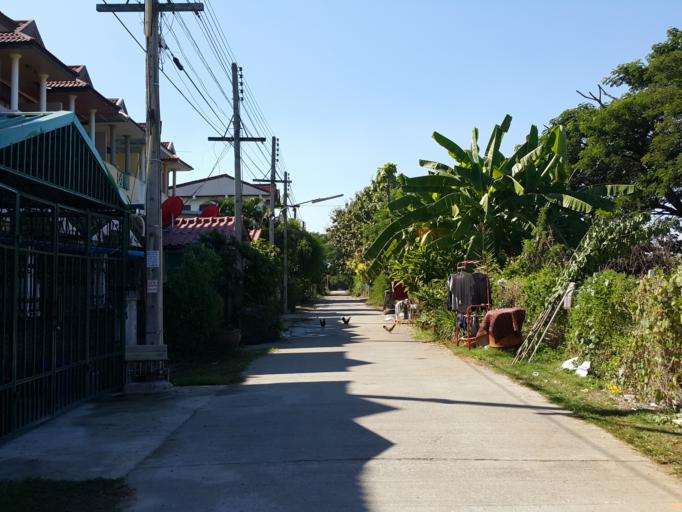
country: TH
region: Chiang Mai
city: Chiang Mai
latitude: 18.7748
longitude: 99.0325
